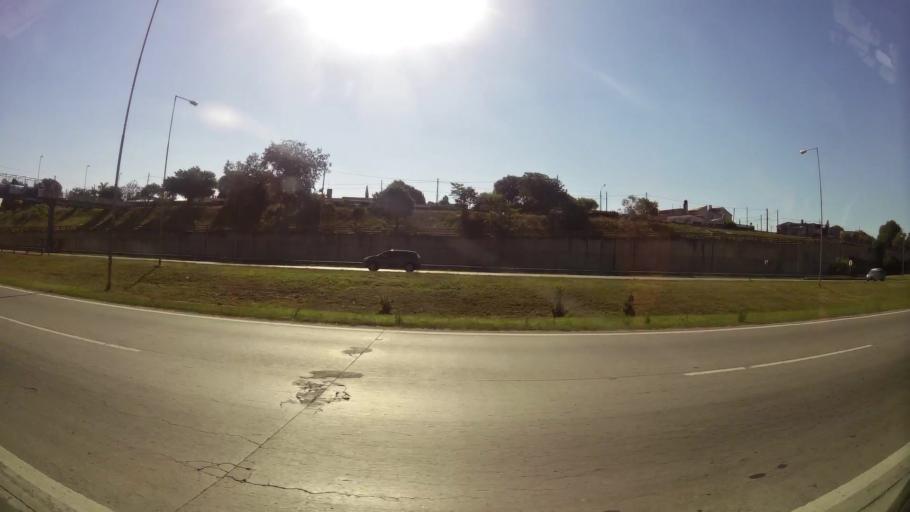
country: AR
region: Cordoba
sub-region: Departamento de Capital
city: Cordoba
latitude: -31.3904
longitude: -64.1266
